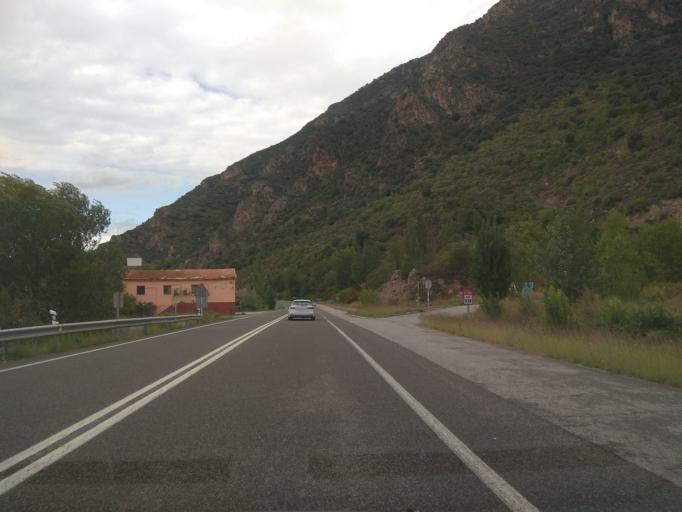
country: ES
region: Catalonia
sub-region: Provincia de Lleida
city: el Pont de Bar
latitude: 42.3592
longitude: 1.5656
